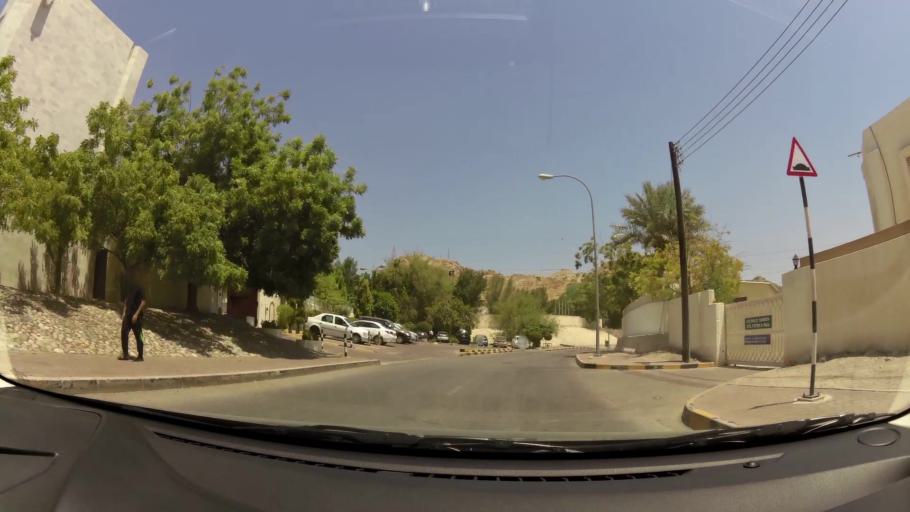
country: OM
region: Muhafazat Masqat
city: Muscat
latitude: 23.6067
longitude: 58.5354
